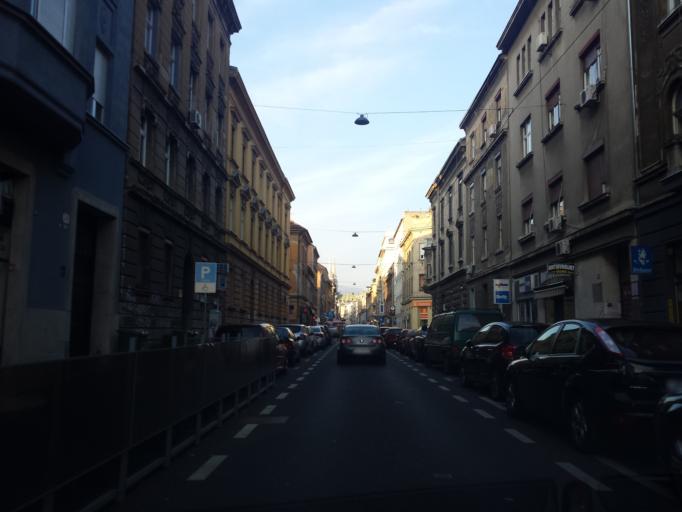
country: HR
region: Grad Zagreb
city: Zagreb - Centar
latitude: 45.8058
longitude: 15.9803
